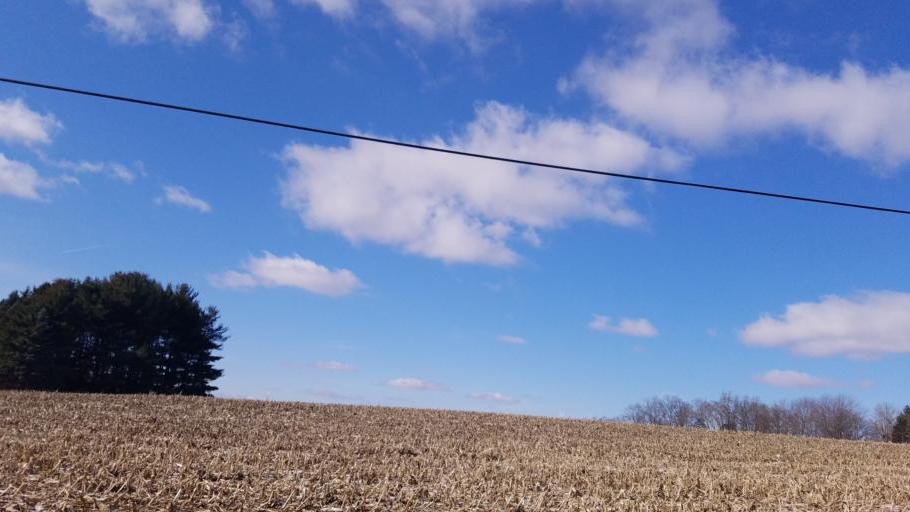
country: US
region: Ohio
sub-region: Richland County
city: Lexington
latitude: 40.6576
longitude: -82.6068
